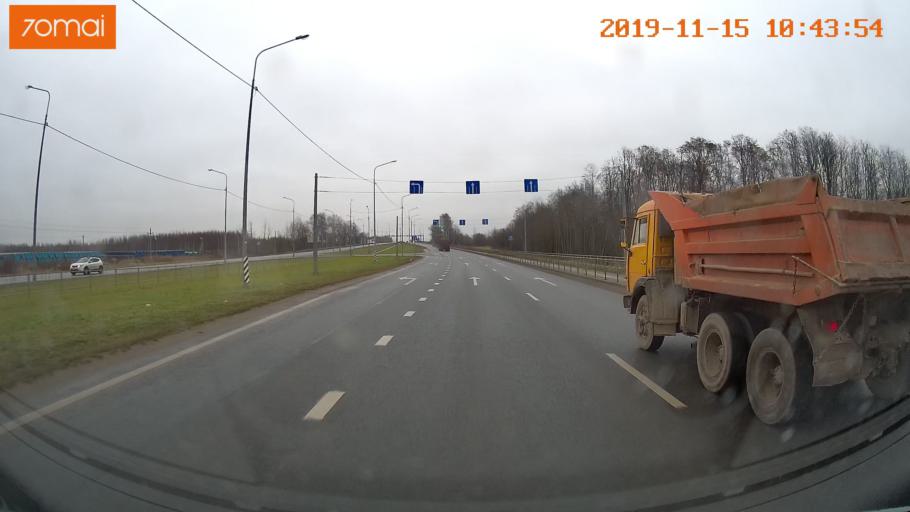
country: RU
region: Vologda
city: Sheksna
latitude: 59.2115
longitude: 38.5456
